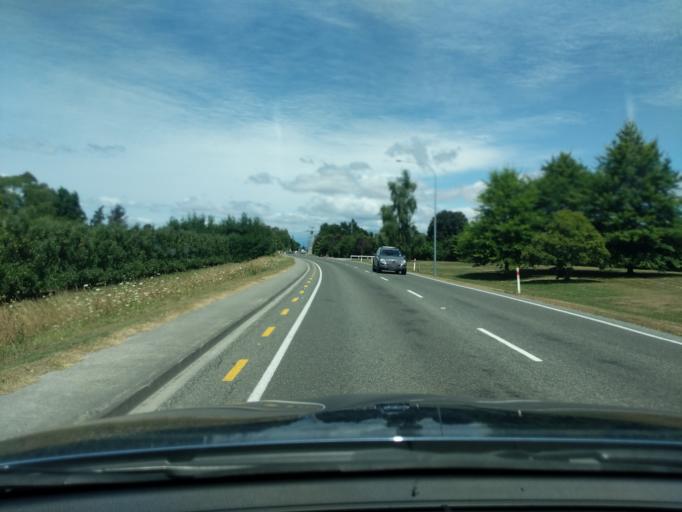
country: NZ
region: Tasman
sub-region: Tasman District
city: Motueka
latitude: -41.0809
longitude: 172.9971
